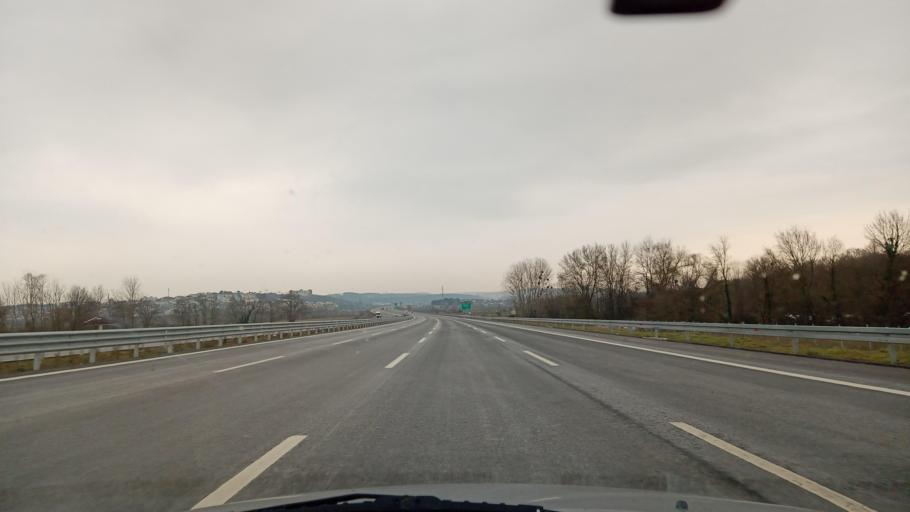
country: TR
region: Sakarya
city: Kazimpasa
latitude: 40.8430
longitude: 30.3075
